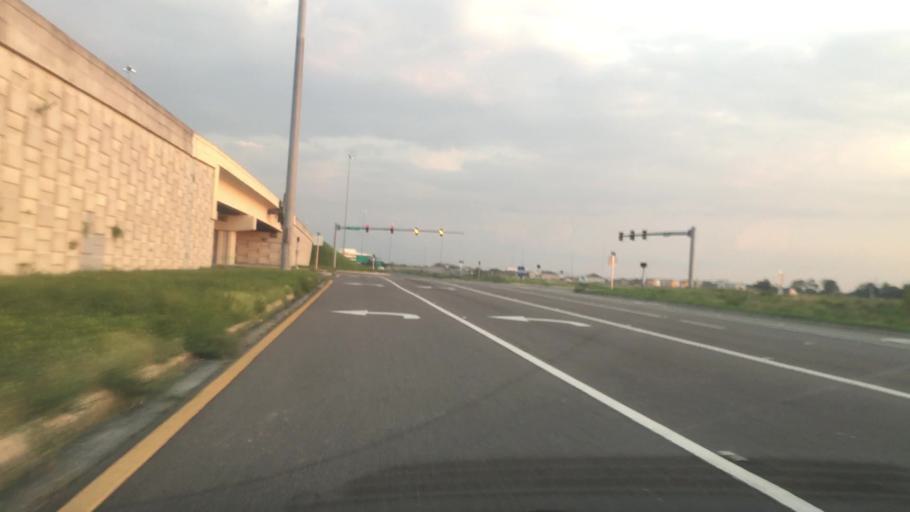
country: US
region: Florida
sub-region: Duval County
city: Jacksonville
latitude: 30.3390
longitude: -81.5525
